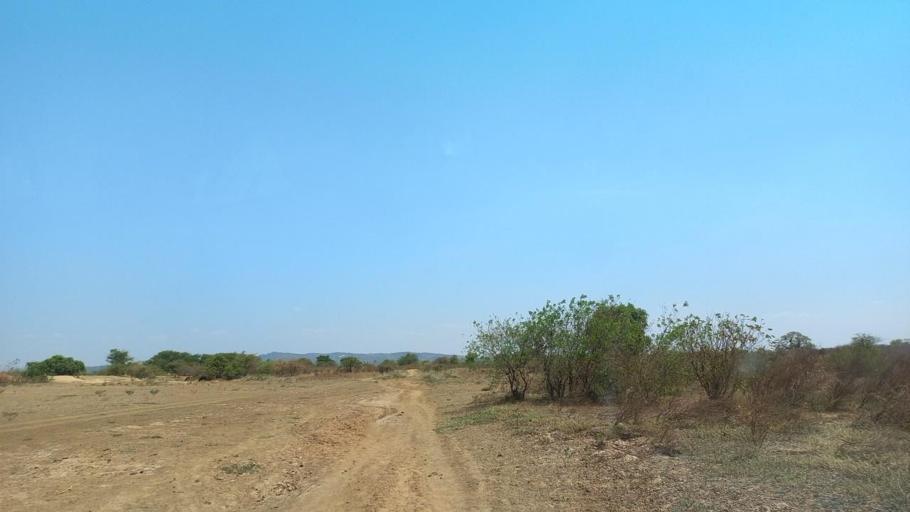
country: ZM
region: Lusaka
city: Luangwa
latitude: -15.5961
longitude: 30.4012
